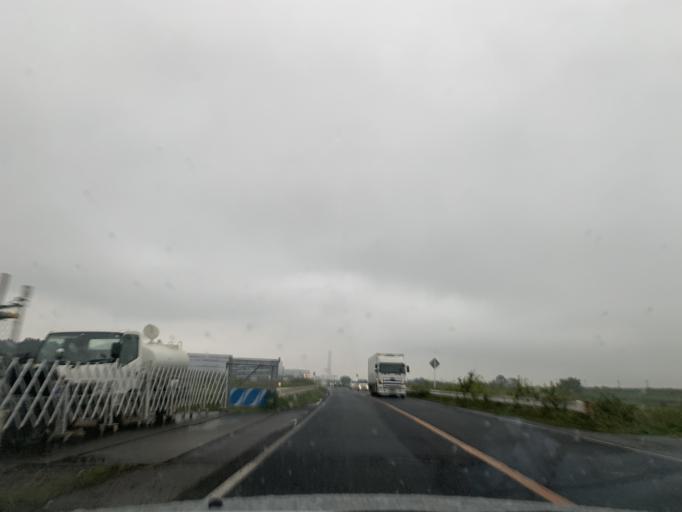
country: JP
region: Chiba
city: Nagareyama
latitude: 35.8938
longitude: 139.8932
